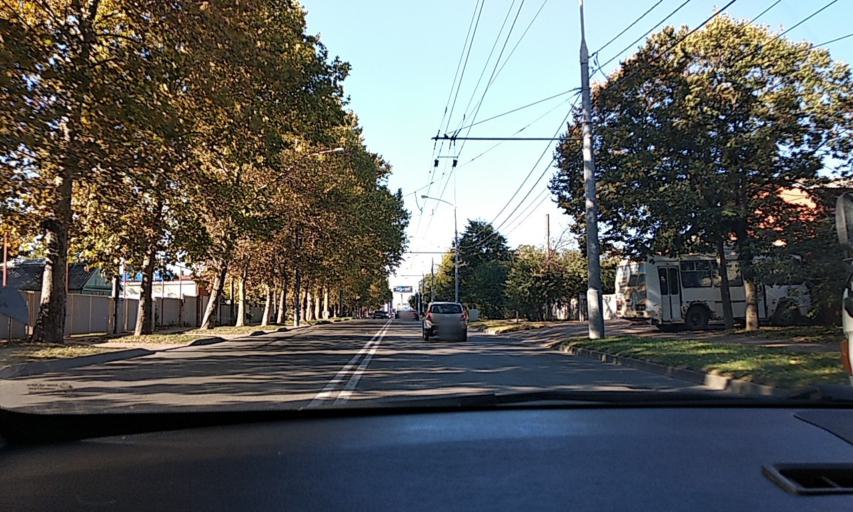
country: RU
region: Krasnodarskiy
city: Pashkovskiy
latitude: 45.0175
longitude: 39.0980
